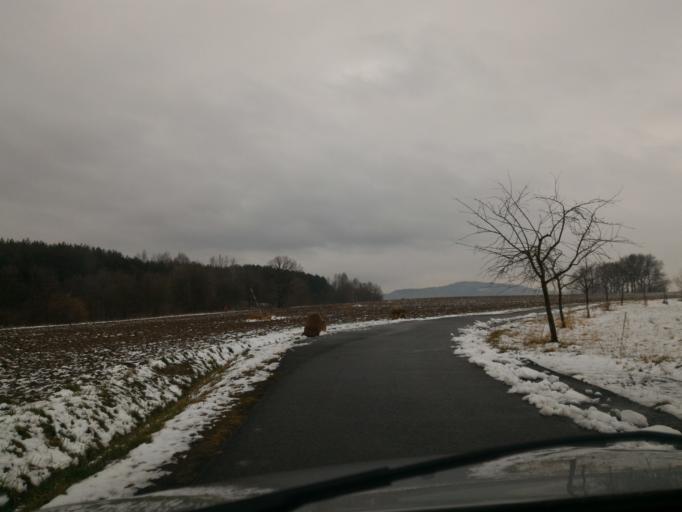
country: DE
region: Saxony
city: Olbersdorf
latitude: 50.8936
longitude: 14.7565
